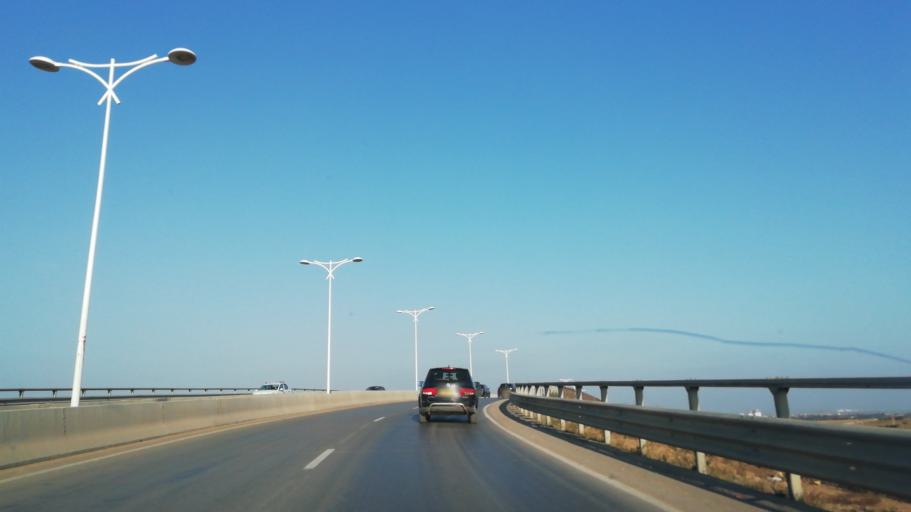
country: DZ
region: Sidi Bel Abbes
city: Sidi Bel Abbes
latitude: 35.1685
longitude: -0.6853
